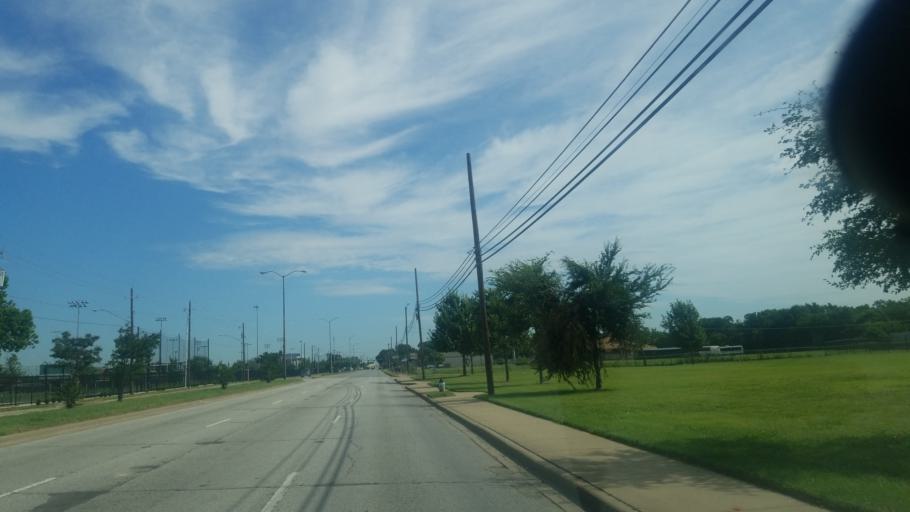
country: US
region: Texas
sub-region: Dallas County
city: Dallas
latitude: 32.7831
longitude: -96.8564
